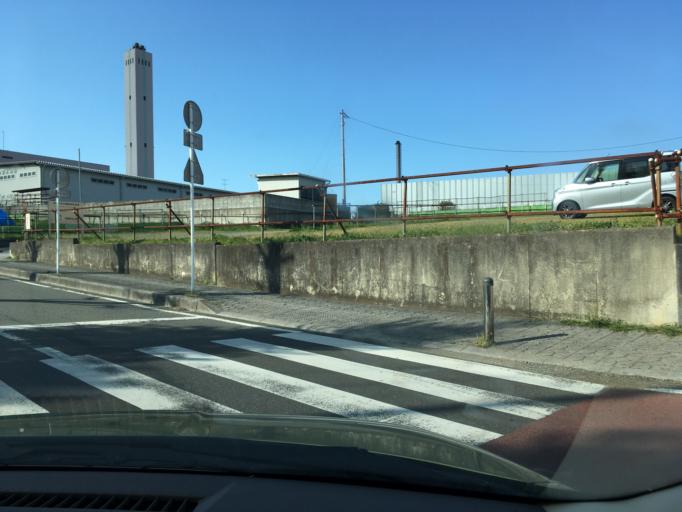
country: JP
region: Tokyo
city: Hachioji
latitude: 35.5827
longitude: 139.3339
